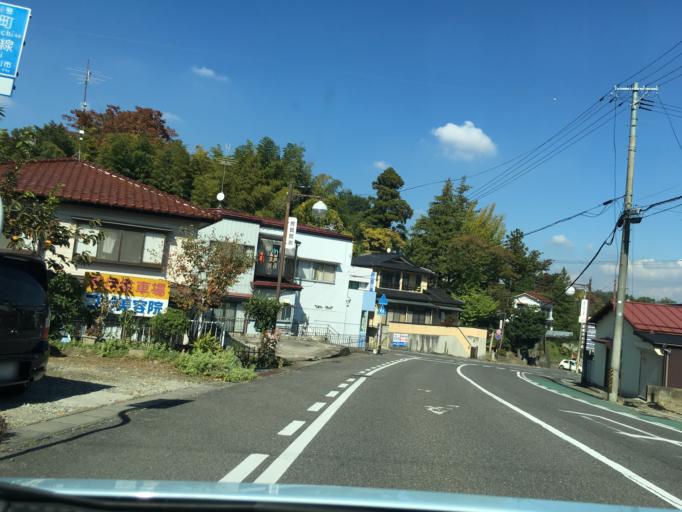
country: JP
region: Fukushima
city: Sukagawa
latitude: 37.2869
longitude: 140.3786
